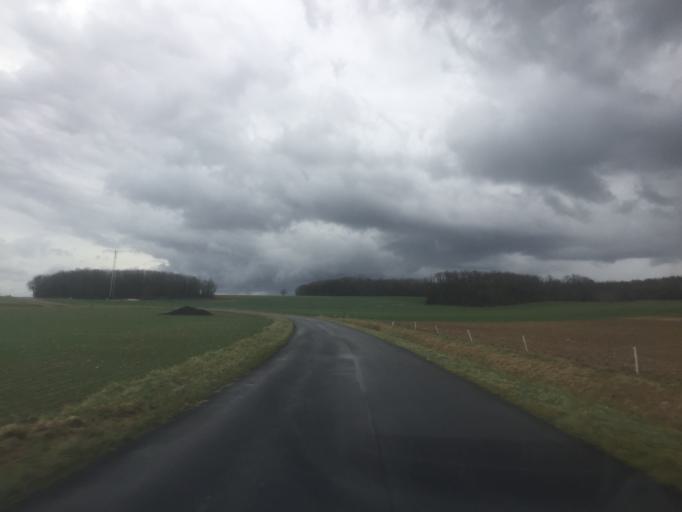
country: FR
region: Franche-Comte
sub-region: Departement de la Haute-Saone
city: Pesmes
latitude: 47.2336
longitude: 5.5797
